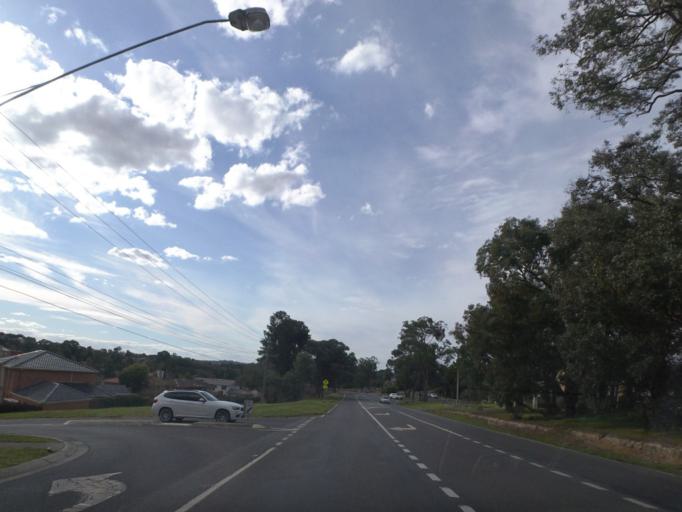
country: AU
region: Victoria
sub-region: Manningham
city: Donvale
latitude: -37.7604
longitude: 145.1738
